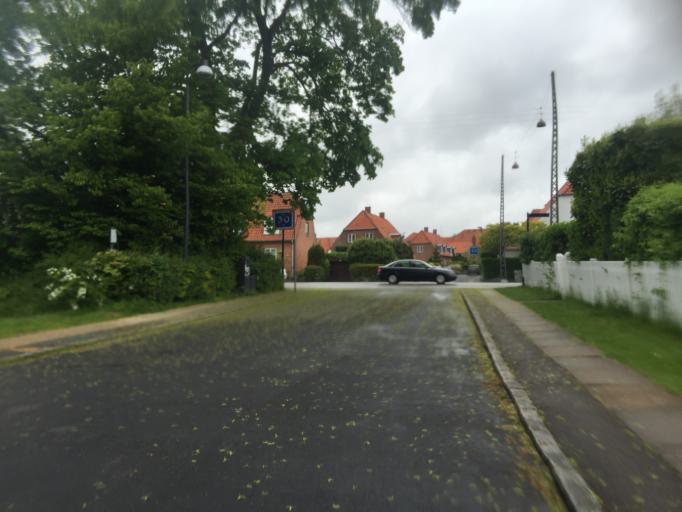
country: DK
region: Capital Region
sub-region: Frederiksberg Kommune
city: Frederiksberg
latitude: 55.6960
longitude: 12.5195
